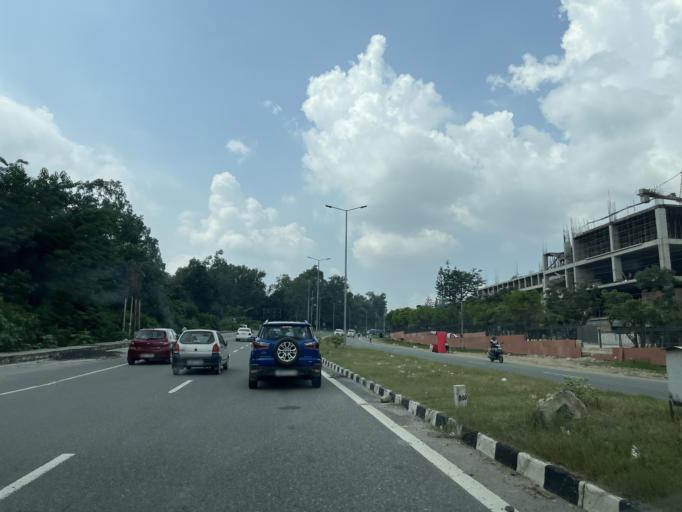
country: IN
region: Uttarakhand
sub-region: Dehradun
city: Raipur
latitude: 30.2659
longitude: 78.0818
